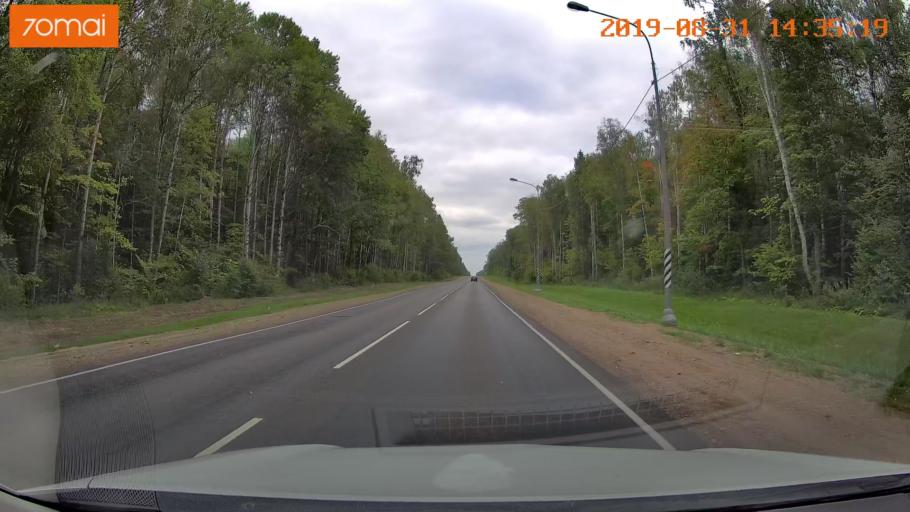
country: RU
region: Smolensk
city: Yekimovichi
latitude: 54.1620
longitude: 33.4529
